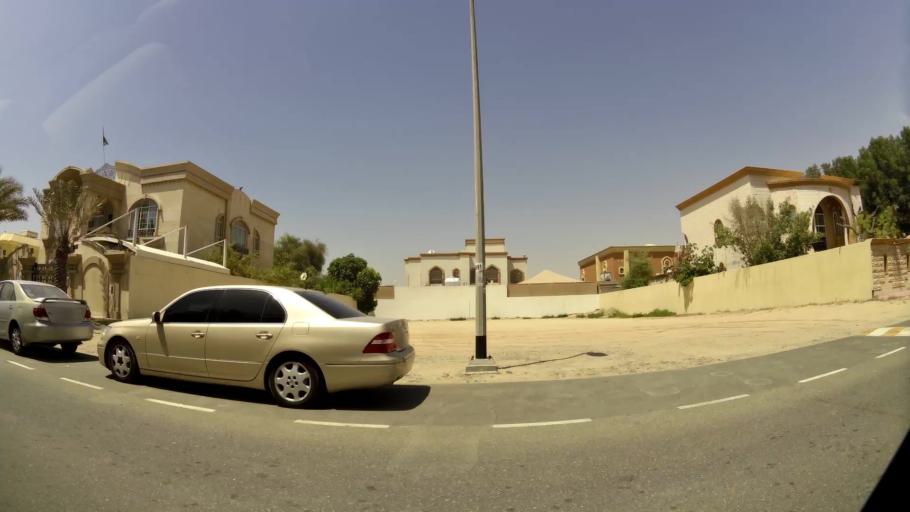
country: AE
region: Dubai
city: Dubai
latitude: 25.1055
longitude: 55.2242
